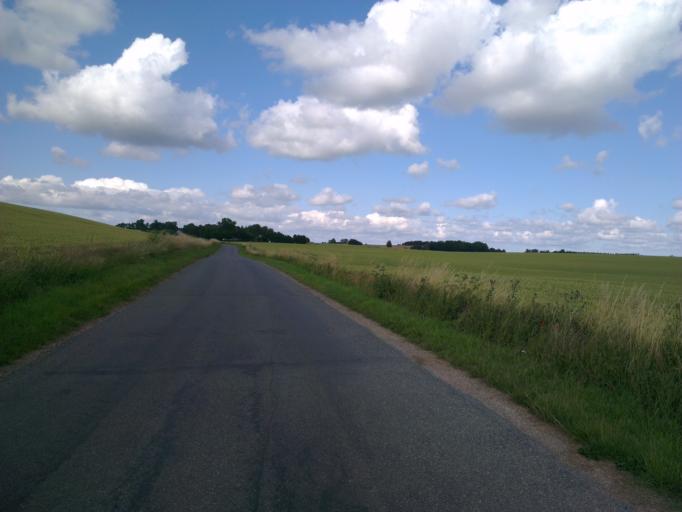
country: DK
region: Capital Region
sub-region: Frederikssund Kommune
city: Skibby
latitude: 55.7421
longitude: 12.0144
